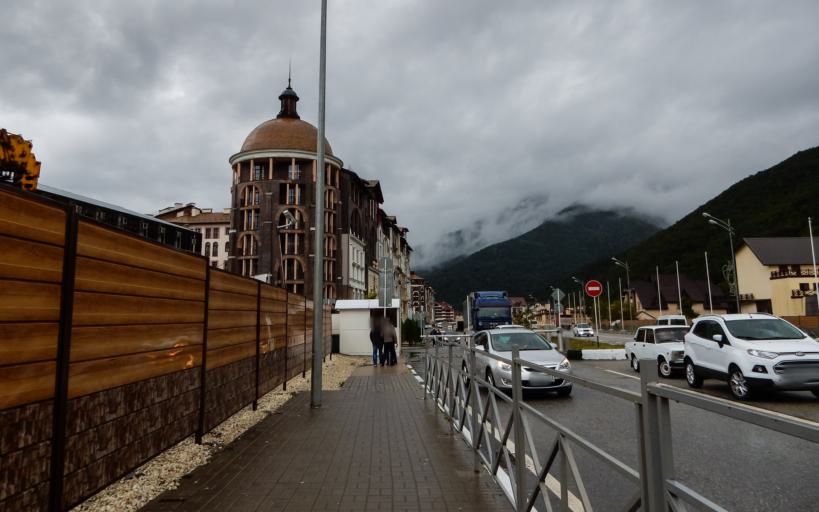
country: RU
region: Krasnodarskiy
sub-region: Sochi City
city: Krasnaya Polyana
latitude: 43.6824
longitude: 40.2713
